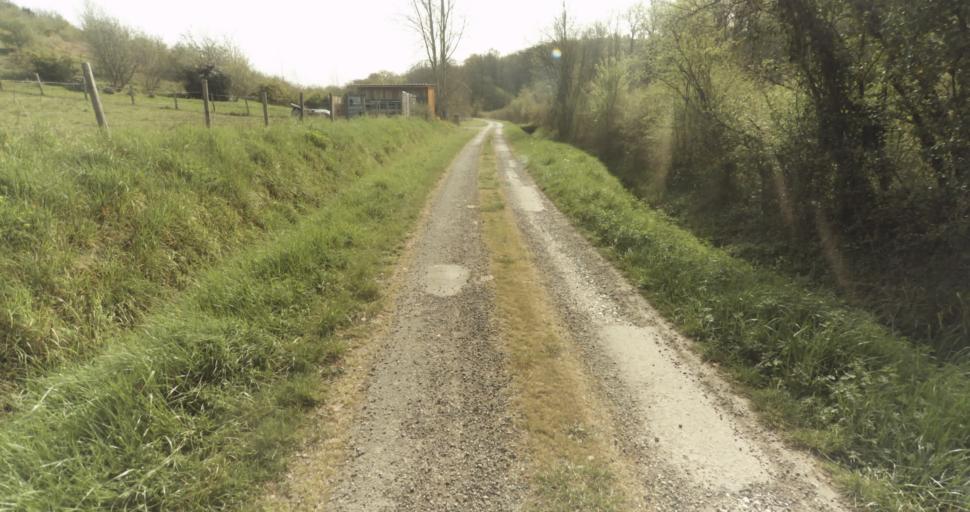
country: FR
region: Midi-Pyrenees
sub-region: Departement du Tarn-et-Garonne
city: Moissac
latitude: 44.1262
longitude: 1.0861
